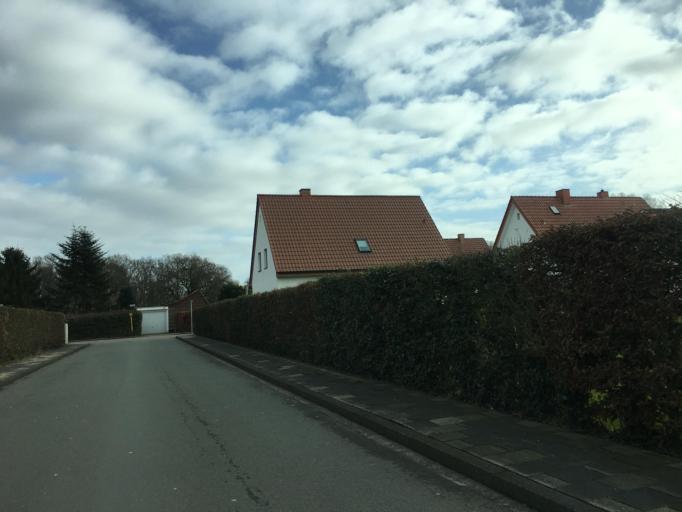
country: DE
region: North Rhine-Westphalia
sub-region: Regierungsbezirk Munster
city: Nordwalde
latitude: 52.0877
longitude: 7.4859
